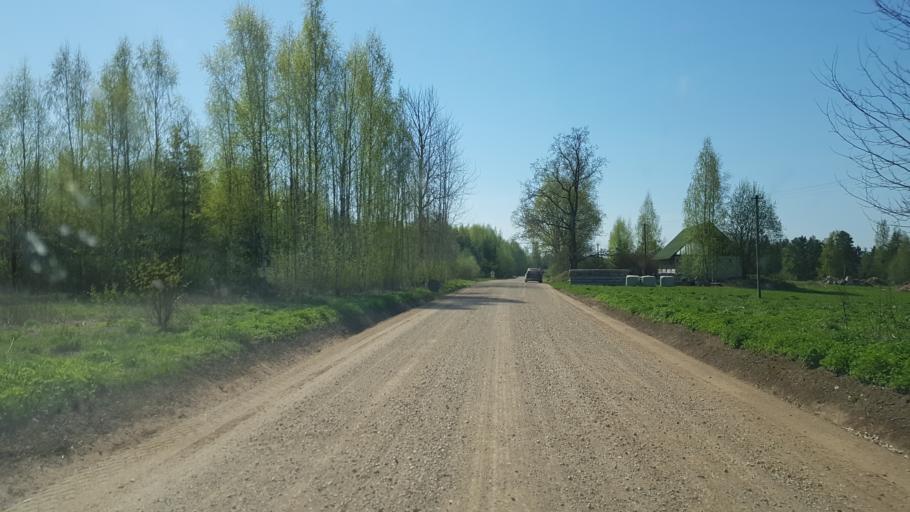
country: EE
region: Polvamaa
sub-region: Polva linn
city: Polva
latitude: 58.1136
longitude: 27.2392
